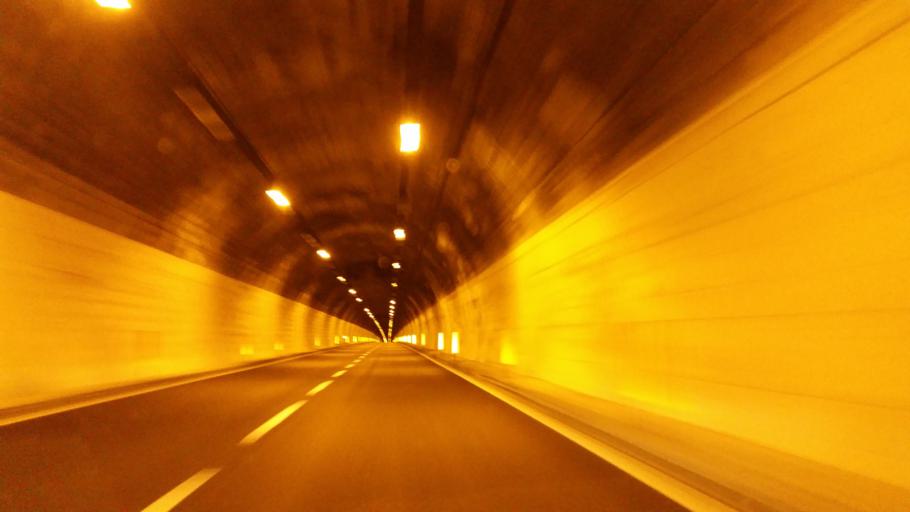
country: IT
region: Liguria
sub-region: Provincia di Savona
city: Alassio
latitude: 44.0045
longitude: 8.1314
